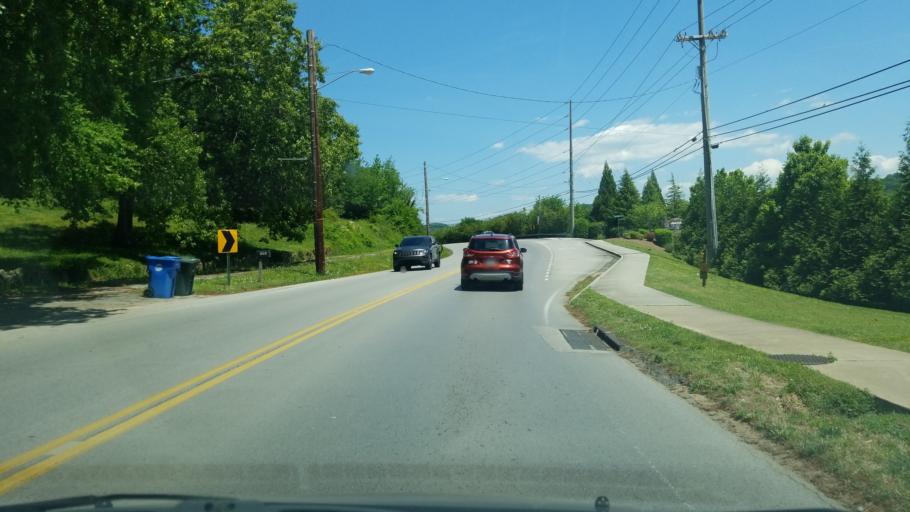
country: US
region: Tennessee
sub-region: Hamilton County
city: Red Bank
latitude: 35.1162
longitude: -85.3189
